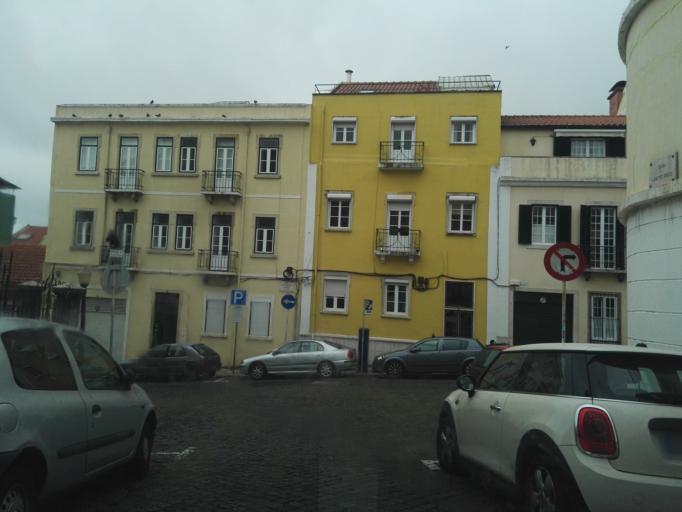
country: PT
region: Setubal
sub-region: Almada
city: Cacilhas
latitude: 38.7058
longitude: -9.1664
